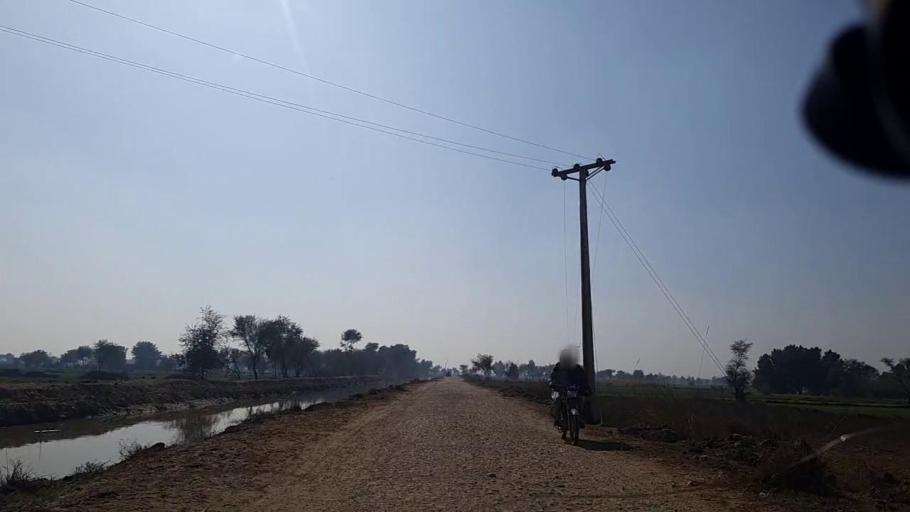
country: PK
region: Sindh
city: Khanpur
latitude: 27.8049
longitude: 69.4129
